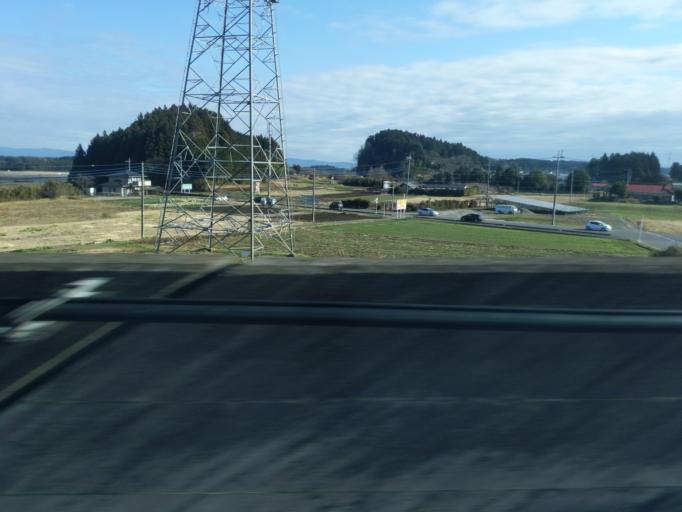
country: JP
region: Tochigi
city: Yaita
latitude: 36.8216
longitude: 139.9597
